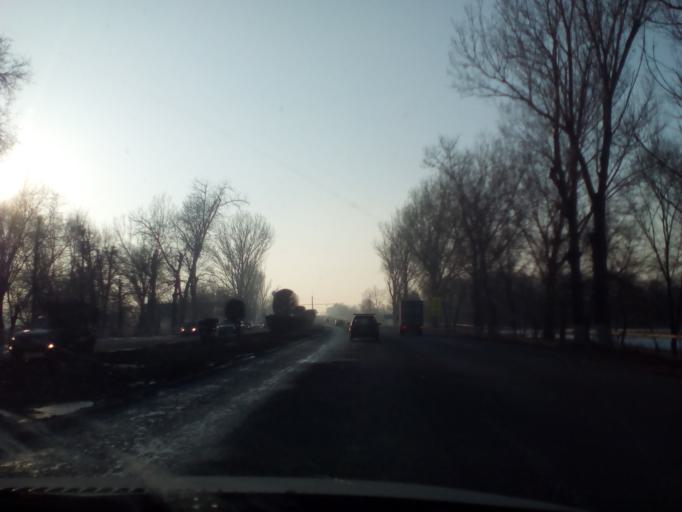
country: KZ
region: Almaty Oblysy
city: Burunday
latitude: 43.2238
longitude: 76.6045
